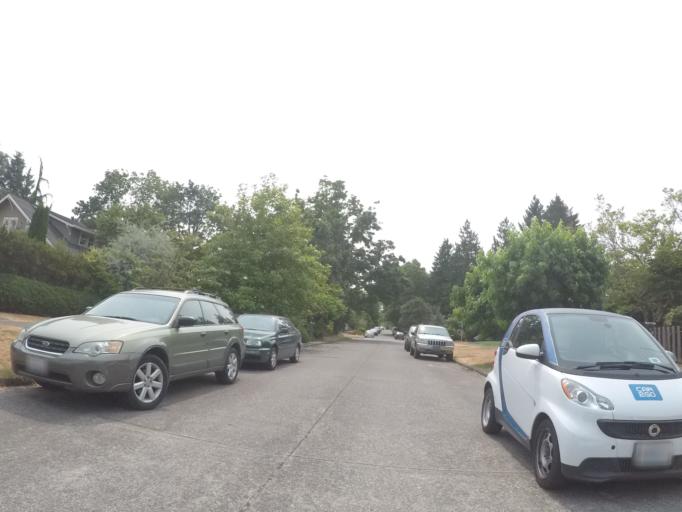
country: US
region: Washington
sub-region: King County
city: Seattle
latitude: 47.5874
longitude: -122.3890
